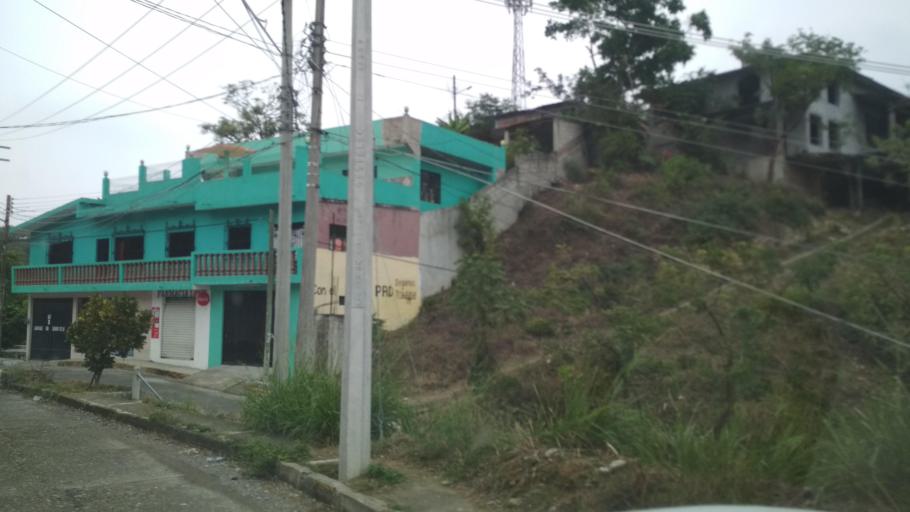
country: MX
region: Veracruz
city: Papantla de Olarte
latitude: 20.4438
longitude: -97.3116
